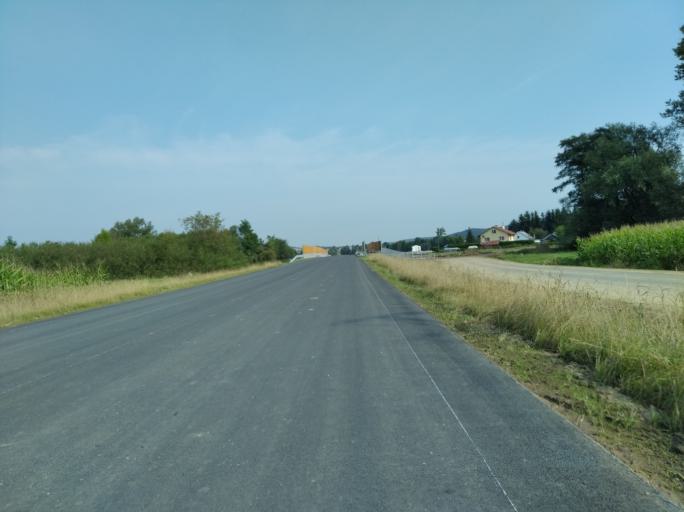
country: PL
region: Subcarpathian Voivodeship
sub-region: Powiat rzeszowski
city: Dynow
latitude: 49.8258
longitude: 22.2414
